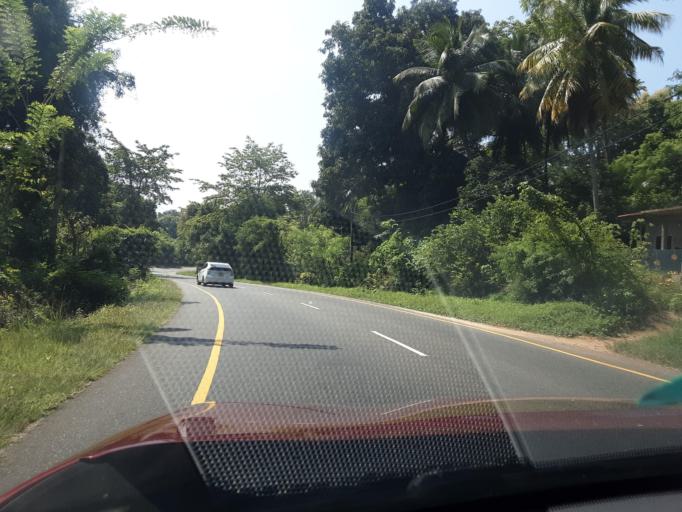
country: LK
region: Uva
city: Badulla
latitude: 7.2852
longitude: 81.0372
